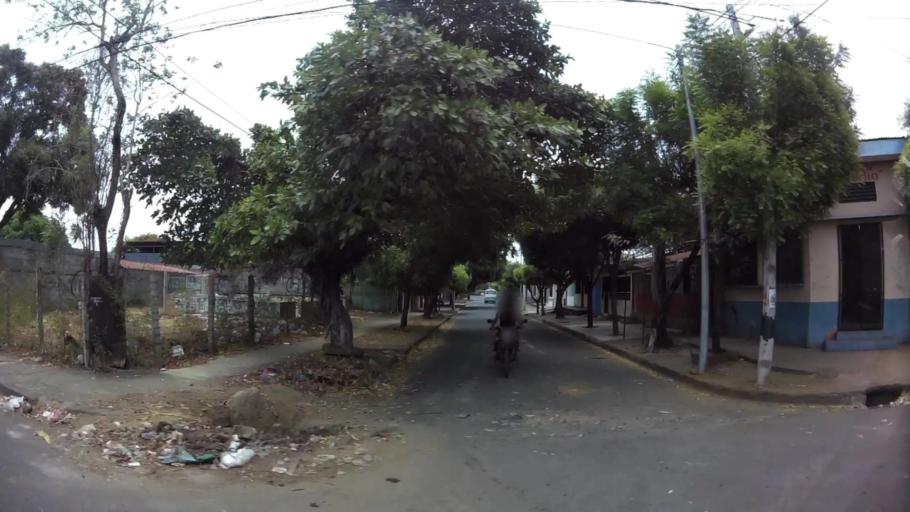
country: NI
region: Managua
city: Managua
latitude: 12.1345
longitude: -86.2929
